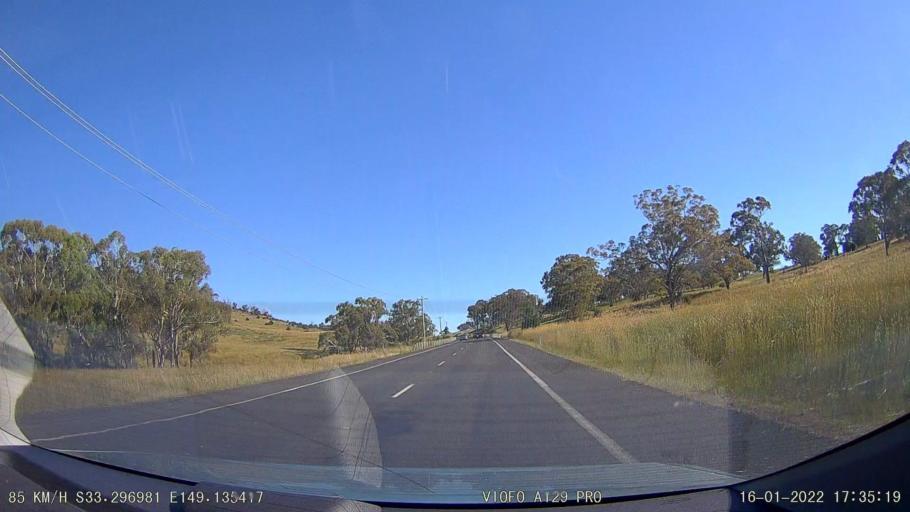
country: AU
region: New South Wales
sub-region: Orange Municipality
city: Orange
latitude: -33.2968
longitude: 149.1355
